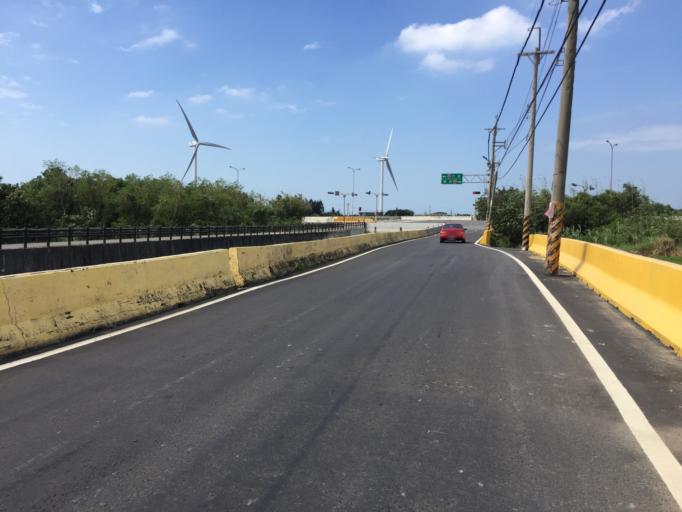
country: TW
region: Taiwan
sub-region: Hsinchu
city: Hsinchu
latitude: 24.7628
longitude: 120.9098
